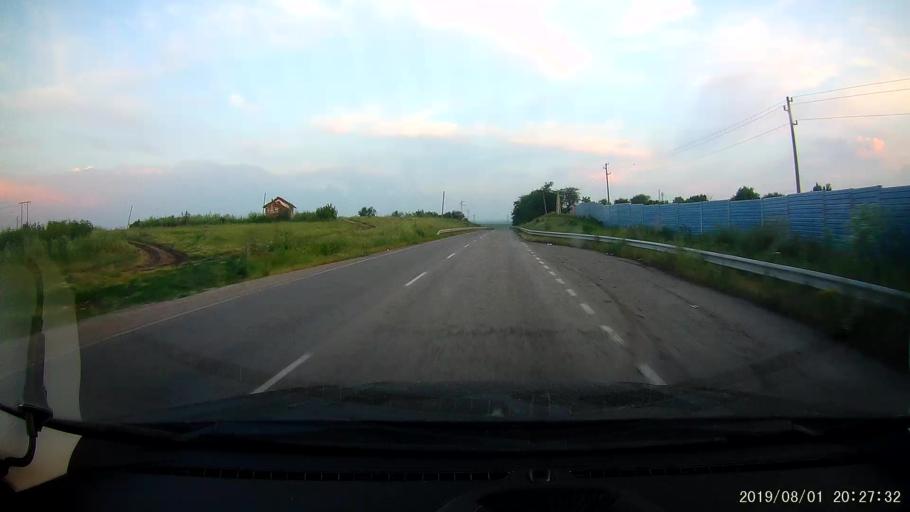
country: BG
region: Yambol
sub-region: Obshtina Elkhovo
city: Elkhovo
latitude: 42.1786
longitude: 26.5844
